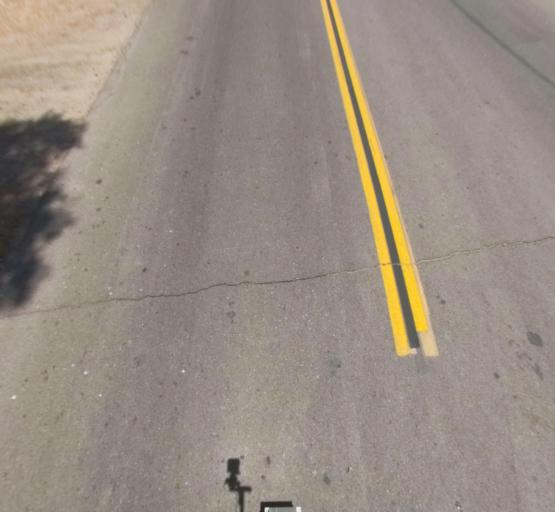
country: US
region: California
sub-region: Madera County
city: Madera
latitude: 36.9830
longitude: -120.0416
